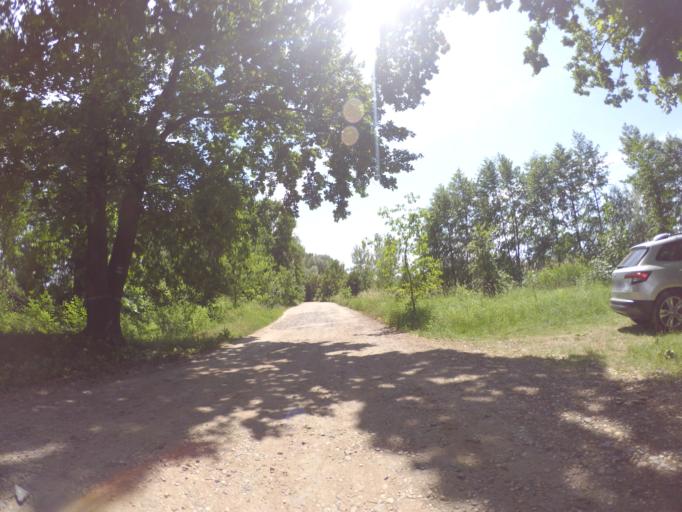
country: CZ
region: Central Bohemia
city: Milovice
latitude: 50.1779
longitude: 14.9014
